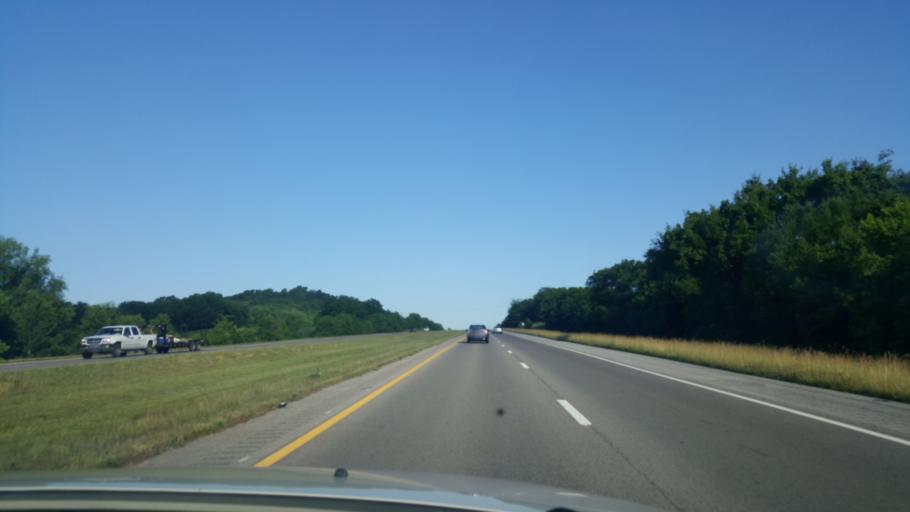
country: US
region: Tennessee
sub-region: Maury County
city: Columbia
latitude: 35.6283
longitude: -87.0881
